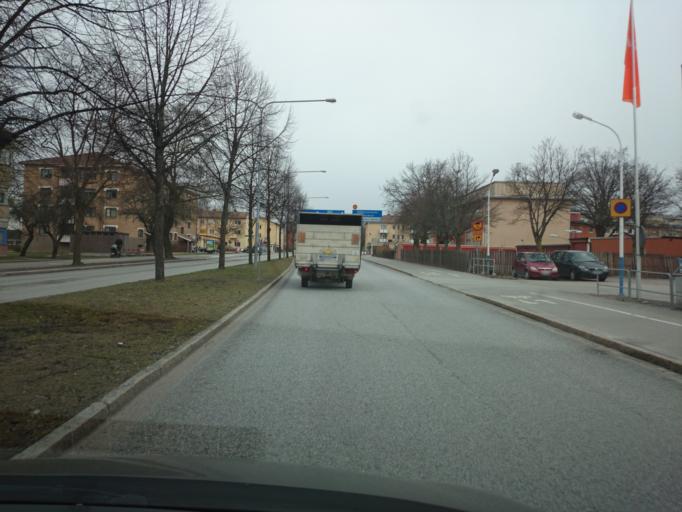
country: SE
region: Uppsala
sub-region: Uppsala Kommun
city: Uppsala
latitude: 59.8691
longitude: 17.6283
